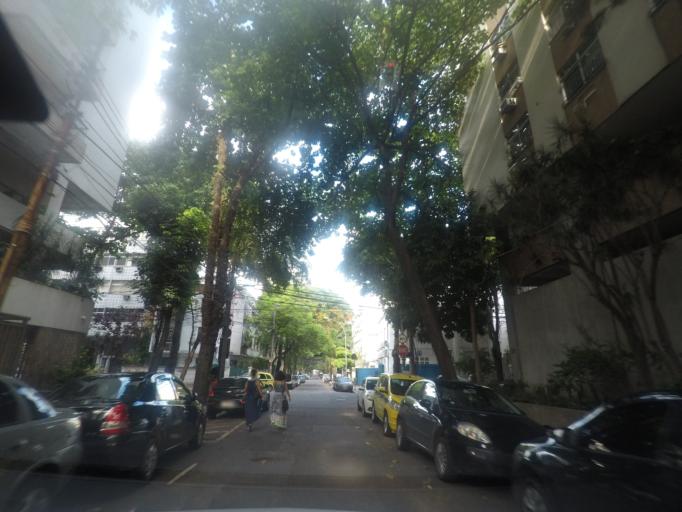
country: BR
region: Rio de Janeiro
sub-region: Rio De Janeiro
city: Rio de Janeiro
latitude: -22.9575
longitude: -43.1972
